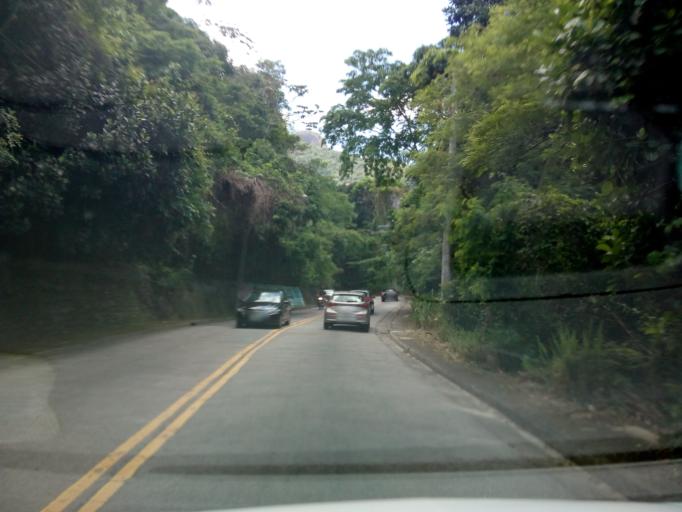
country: BR
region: Rio de Janeiro
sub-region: Rio De Janeiro
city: Rio de Janeiro
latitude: -22.9834
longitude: -43.2976
